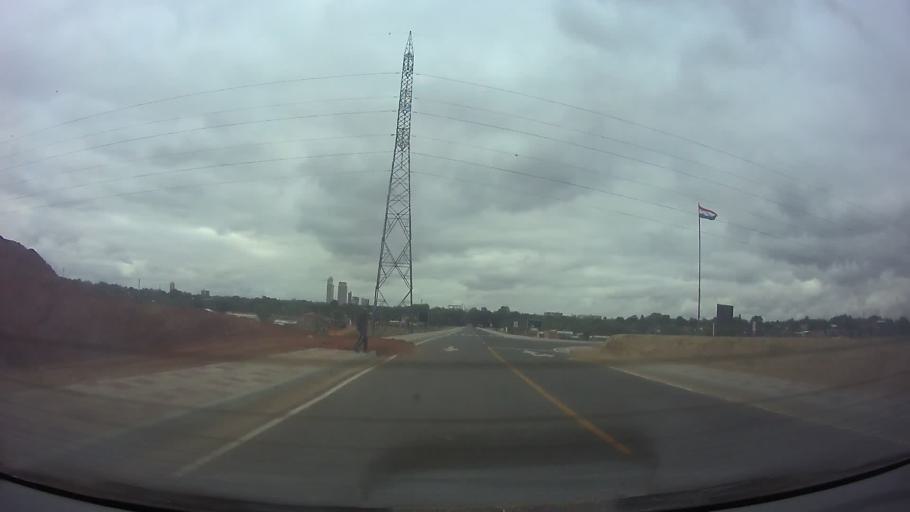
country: PY
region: Asuncion
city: Asuncion
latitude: -25.2494
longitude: -57.5919
